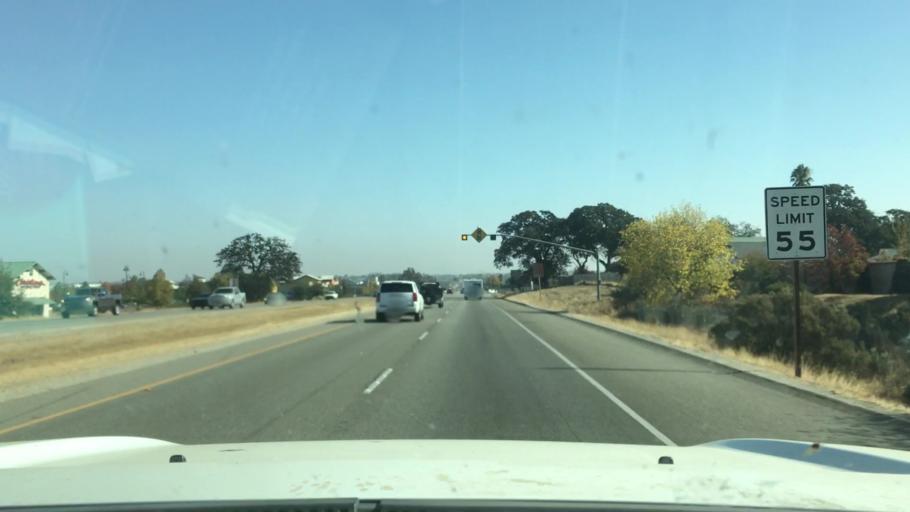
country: US
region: California
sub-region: San Luis Obispo County
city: Paso Robles
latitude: 35.6445
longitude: -120.6629
